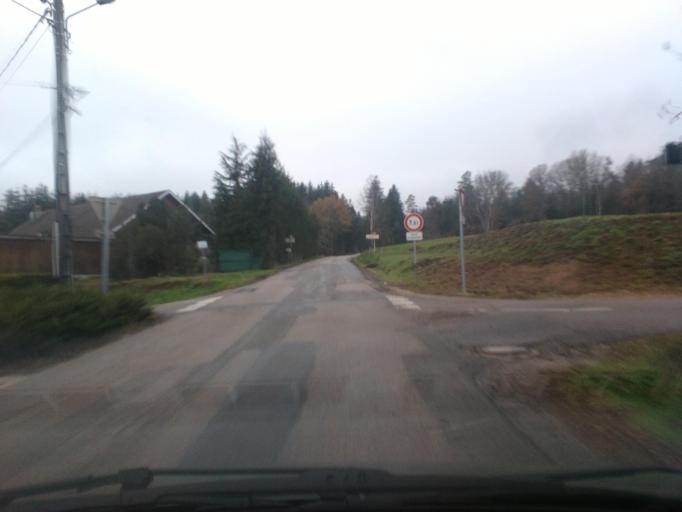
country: FR
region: Lorraine
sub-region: Departement des Vosges
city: Saint-Leonard
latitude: 48.2431
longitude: 6.9345
